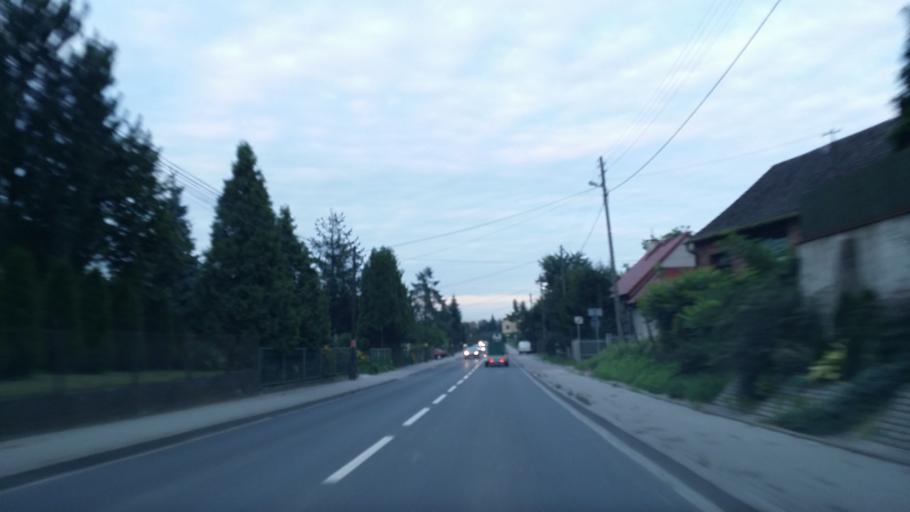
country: PL
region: Lesser Poland Voivodeship
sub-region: Powiat krakowski
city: Liszki
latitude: 50.0389
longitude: 19.7713
